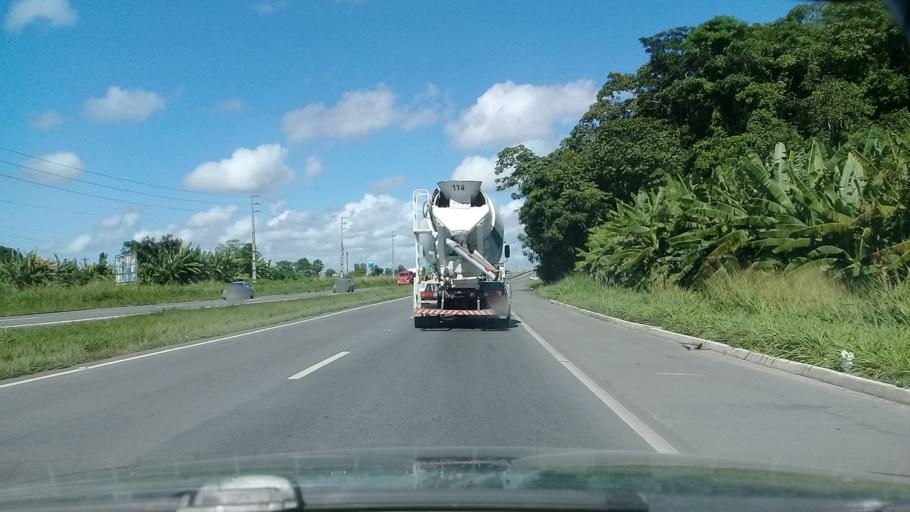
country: BR
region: Pernambuco
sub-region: Jaboatao Dos Guararapes
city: Jaboatao
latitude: -8.1973
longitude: -34.9773
